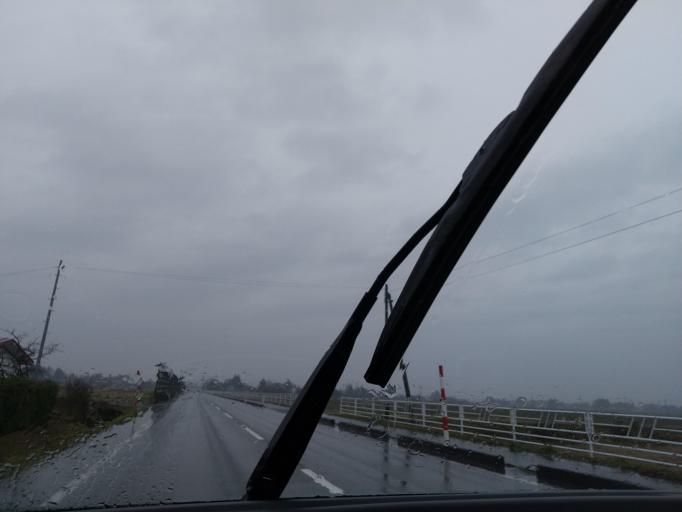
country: JP
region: Iwate
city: Hanamaki
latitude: 39.4380
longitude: 141.0973
